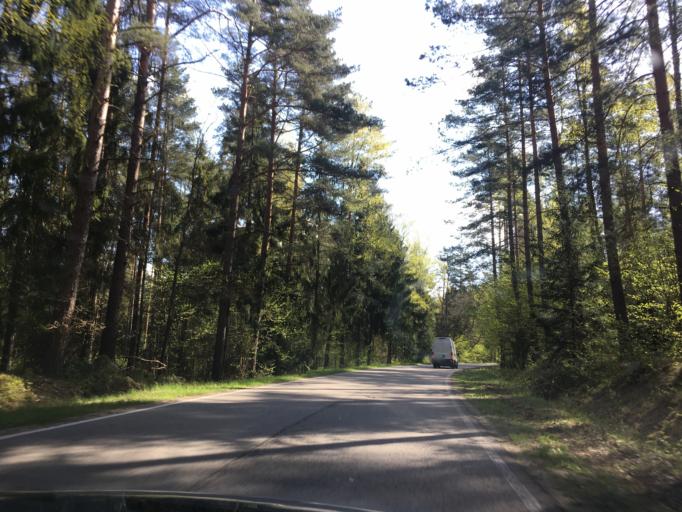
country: PL
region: Warmian-Masurian Voivodeship
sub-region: Powiat piski
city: Ruciane-Nida
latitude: 53.6781
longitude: 21.5916
